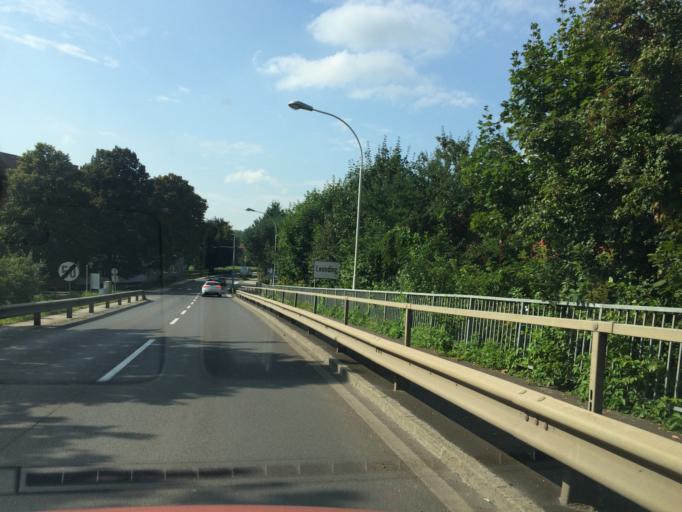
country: AT
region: Upper Austria
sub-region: Politischer Bezirk Linz-Land
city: Leonding
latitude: 48.2750
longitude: 14.2546
